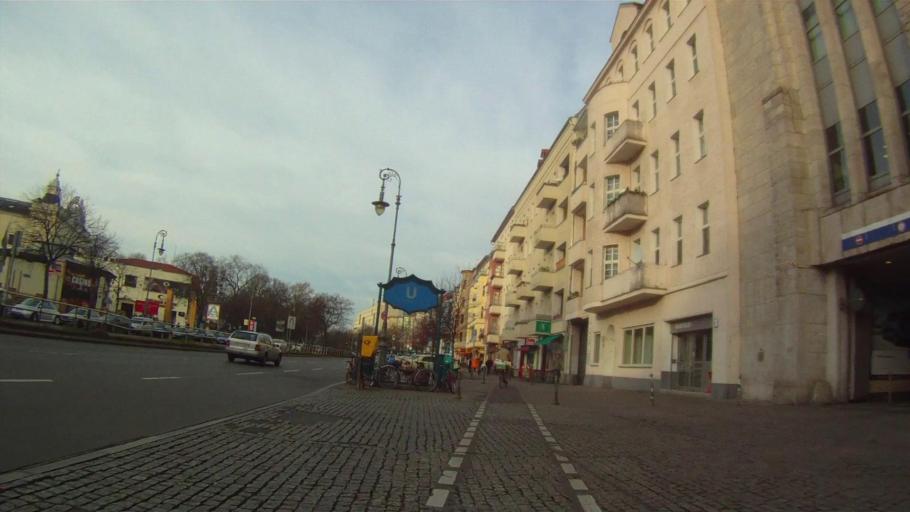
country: DE
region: Berlin
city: Berlin Treptow
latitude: 52.4869
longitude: 13.4232
